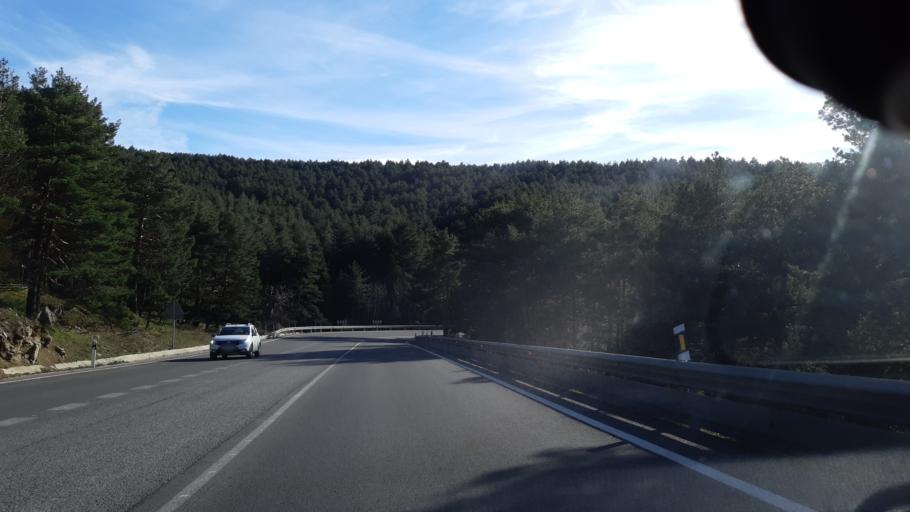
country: ES
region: Madrid
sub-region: Provincia de Madrid
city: Guadarrama
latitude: 40.7083
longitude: -4.1518
